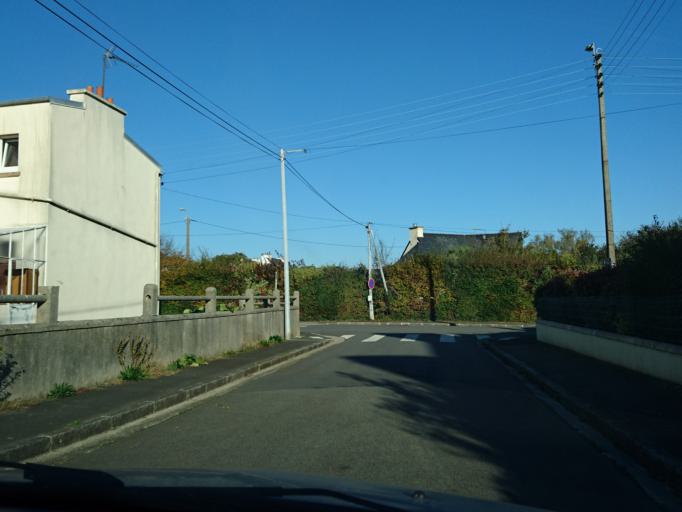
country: FR
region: Brittany
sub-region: Departement du Finistere
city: Brest
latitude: 48.4147
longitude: -4.4520
